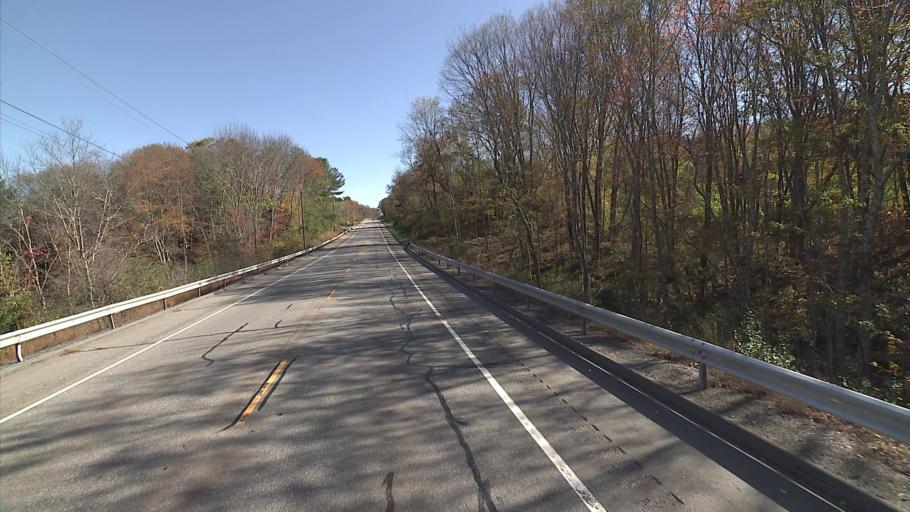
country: US
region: Connecticut
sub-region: Windham County
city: Danielson
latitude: 41.7896
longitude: -71.8633
